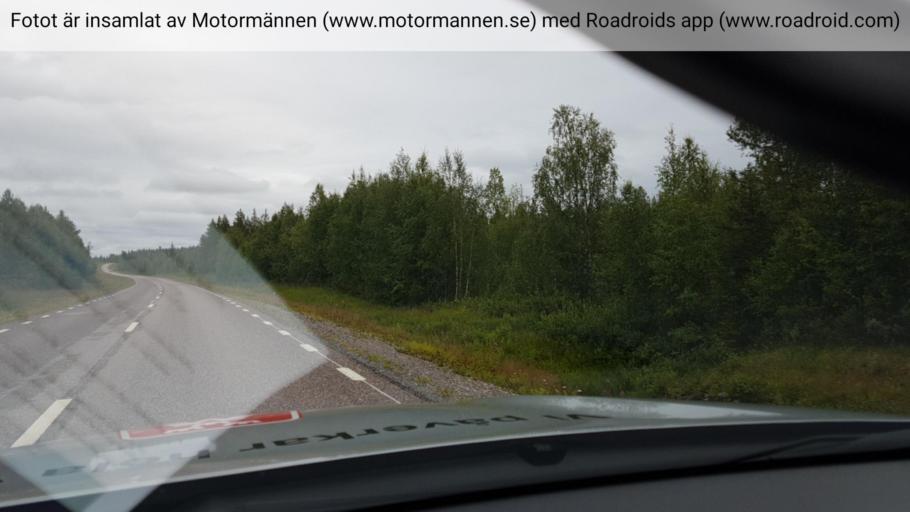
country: SE
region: Norrbotten
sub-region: Gallivare Kommun
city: Gaellivare
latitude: 67.0699
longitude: 21.4989
